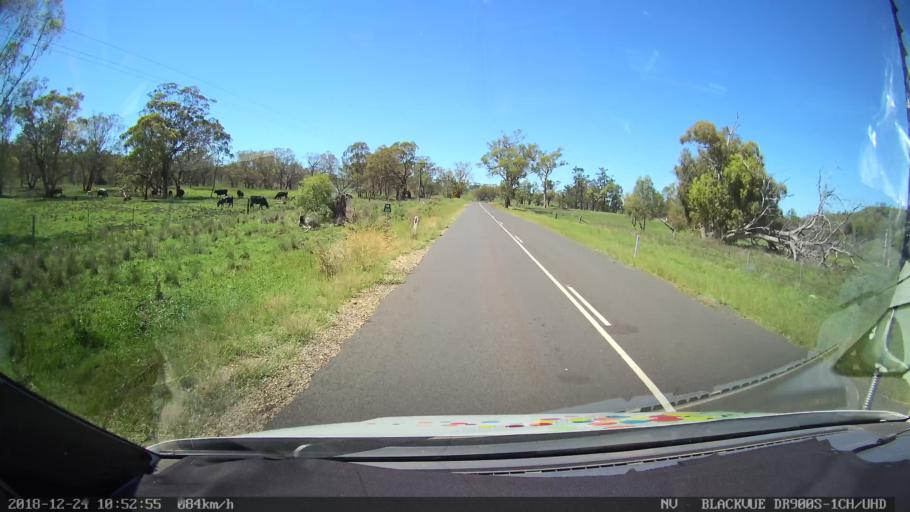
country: AU
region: New South Wales
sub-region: Upper Hunter Shire
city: Merriwa
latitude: -31.9863
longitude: 150.4227
